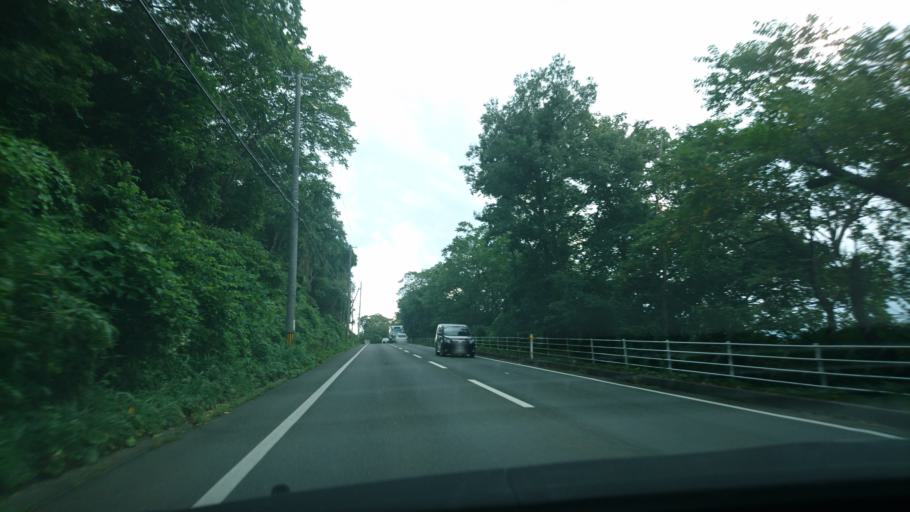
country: JP
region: Iwate
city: Kitakami
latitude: 39.2651
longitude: 141.1254
